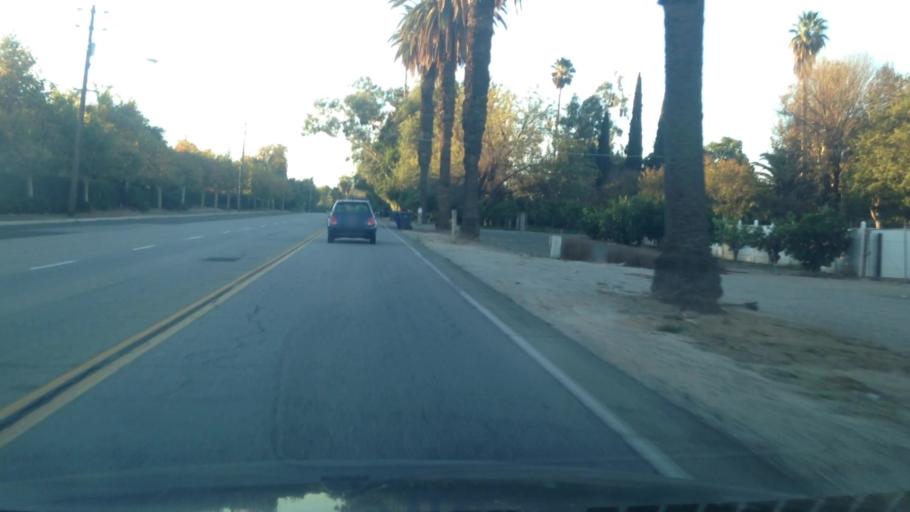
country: US
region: California
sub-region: Riverside County
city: Riverside
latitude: 33.9176
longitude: -117.3835
